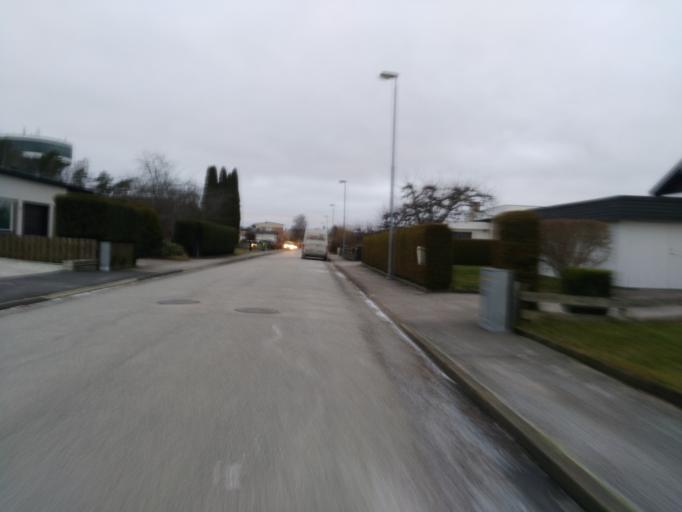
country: SE
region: Vaestra Goetaland
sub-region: Lidkopings Kommun
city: Lidkoping
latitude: 58.4900
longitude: 13.1642
